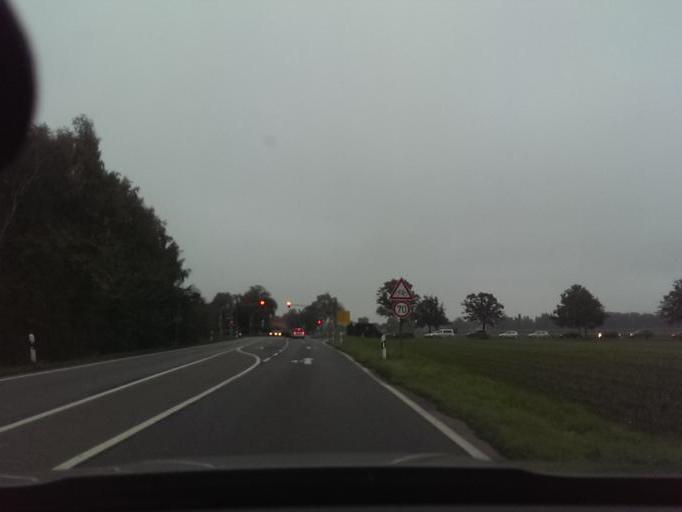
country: DE
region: Lower Saxony
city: Garbsen-Mitte
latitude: 52.4432
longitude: 9.6388
